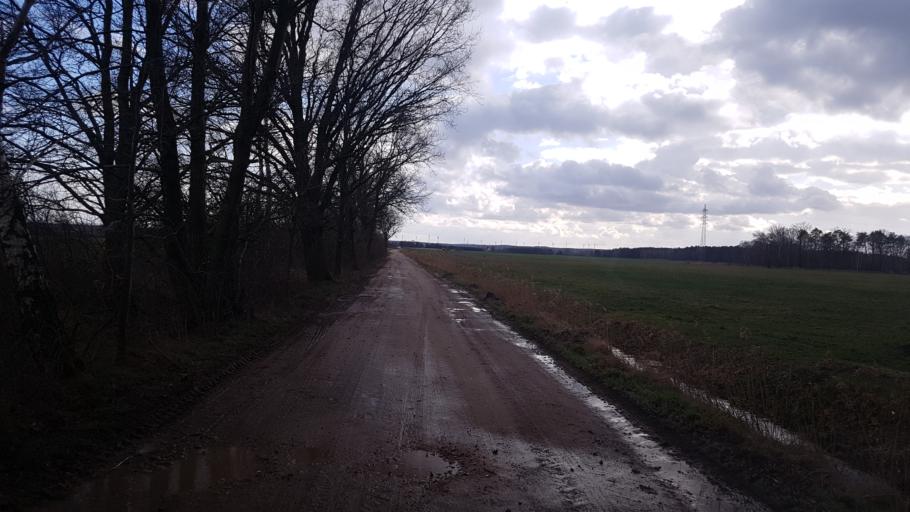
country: DE
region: Brandenburg
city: Sallgast
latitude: 51.6258
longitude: 13.8562
